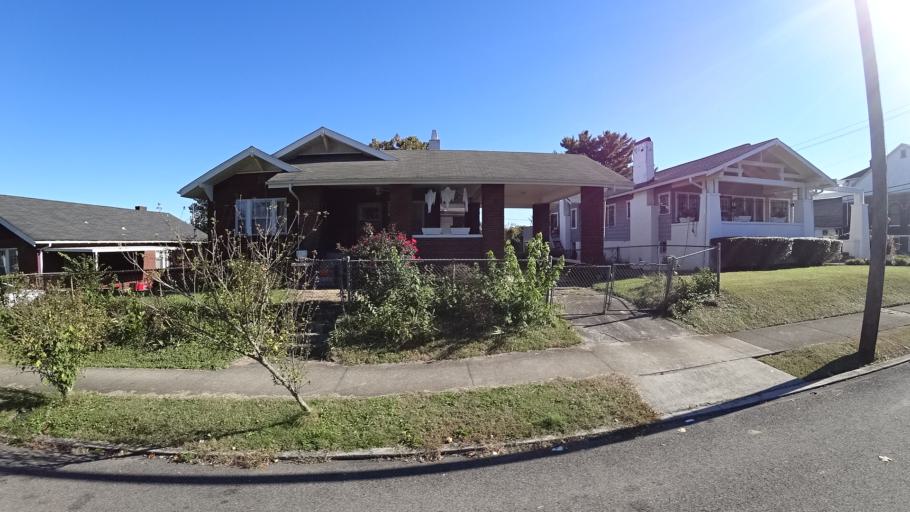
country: US
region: Tennessee
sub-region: Knox County
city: Knoxville
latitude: 35.9838
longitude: -83.8942
